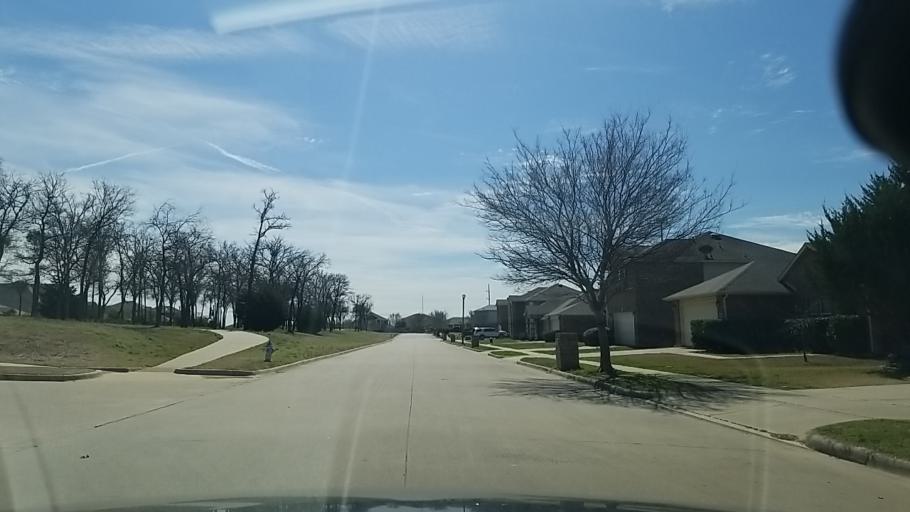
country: US
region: Texas
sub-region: Denton County
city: Corinth
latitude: 33.1529
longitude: -97.1018
